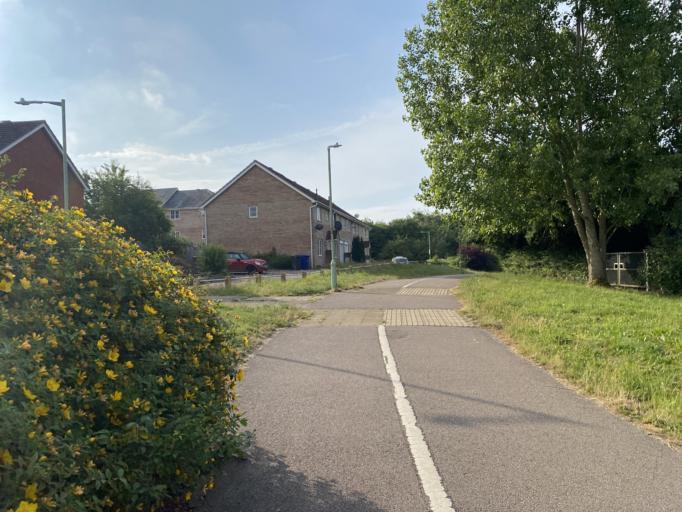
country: GB
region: England
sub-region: Suffolk
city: Haverhill
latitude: 52.0798
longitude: 0.4497
